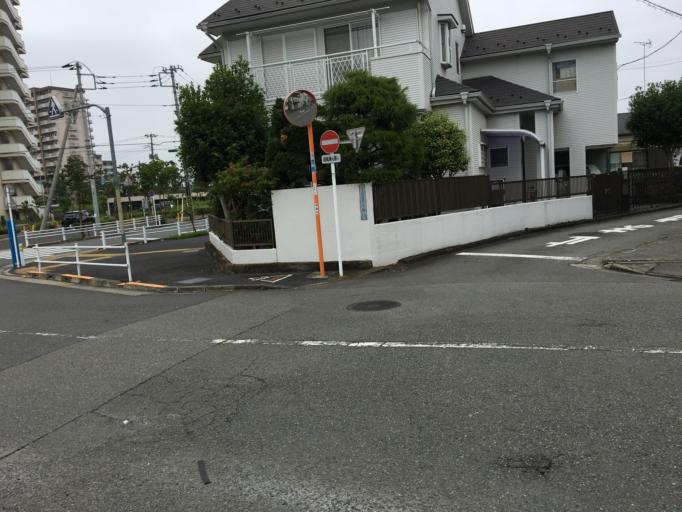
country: JP
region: Tokyo
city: Fussa
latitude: 35.7118
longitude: 139.3371
